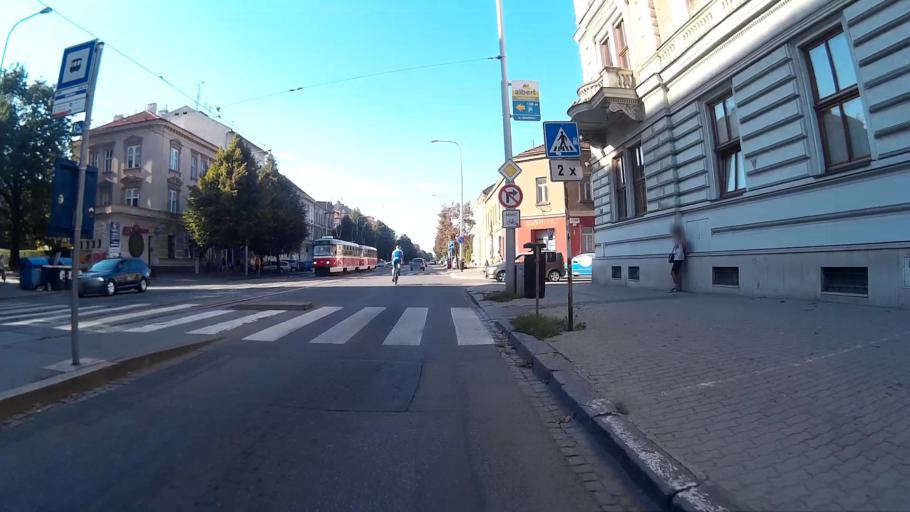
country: CZ
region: South Moravian
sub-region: Mesto Brno
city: Brno
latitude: 49.2103
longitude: 16.6030
